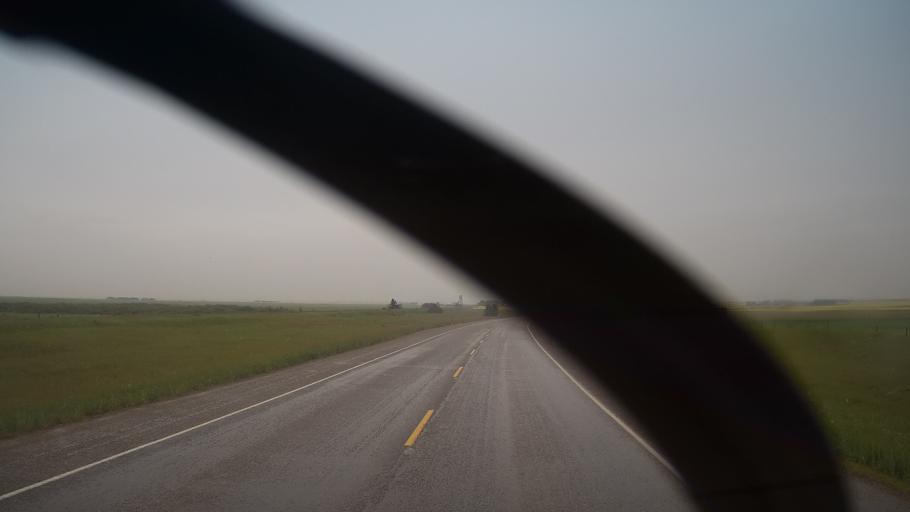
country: CA
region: Saskatchewan
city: Wilkie
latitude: 52.1900
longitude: -108.4173
